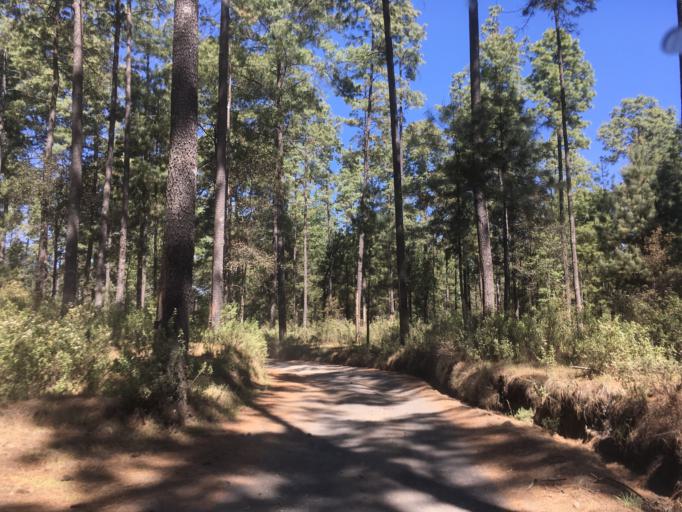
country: MX
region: Michoacan
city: Angahuan
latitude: 19.4632
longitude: -102.2137
